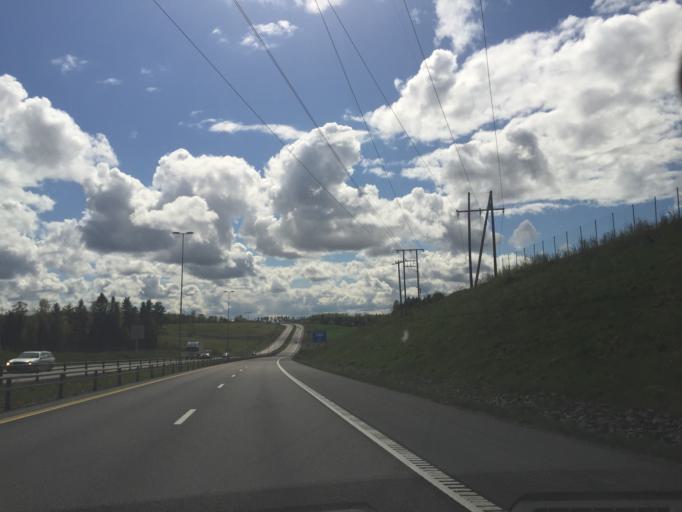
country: NO
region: Akershus
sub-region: Eidsvoll
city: Raholt
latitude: 60.2436
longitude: 11.1815
